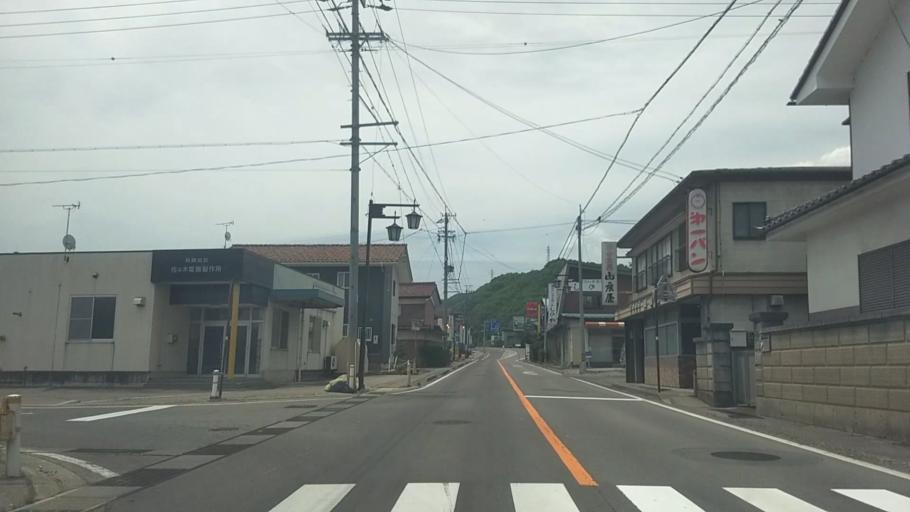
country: JP
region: Nagano
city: Saku
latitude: 36.1323
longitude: 138.4712
